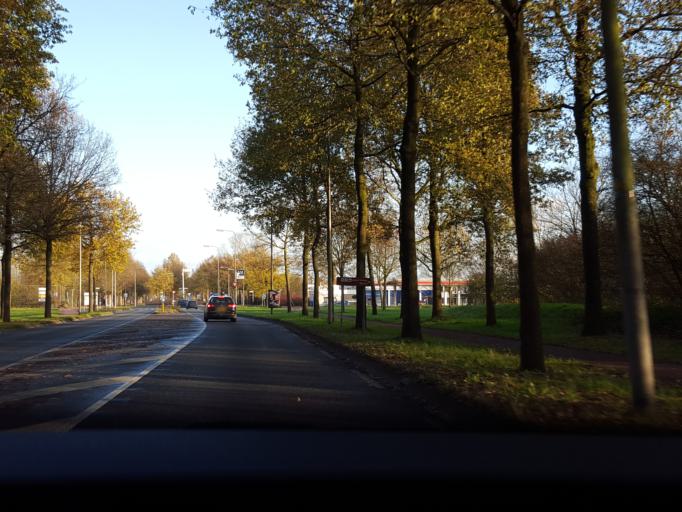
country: NL
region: Gelderland
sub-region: Gemeente Zutphen
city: Zutphen
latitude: 52.1273
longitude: 6.2077
